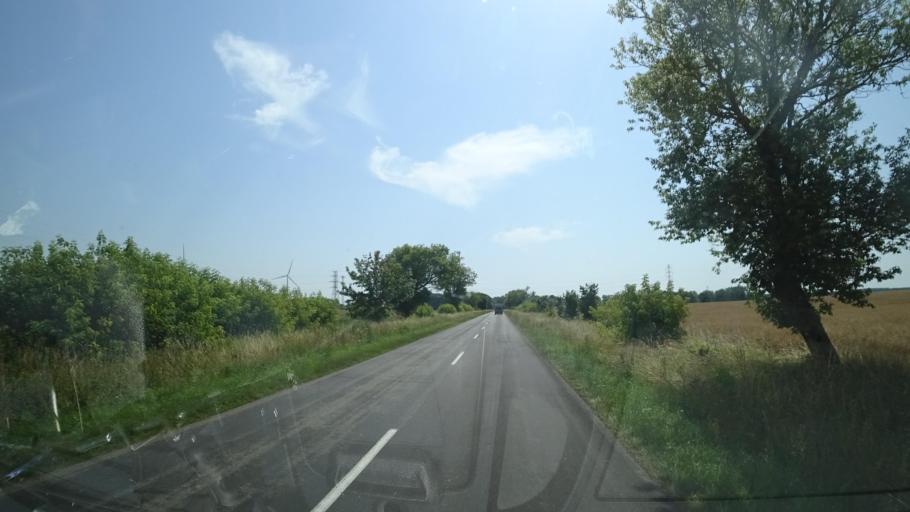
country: PL
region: West Pomeranian Voivodeship
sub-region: Powiat lobeski
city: Lobez
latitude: 53.7212
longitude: 15.5872
